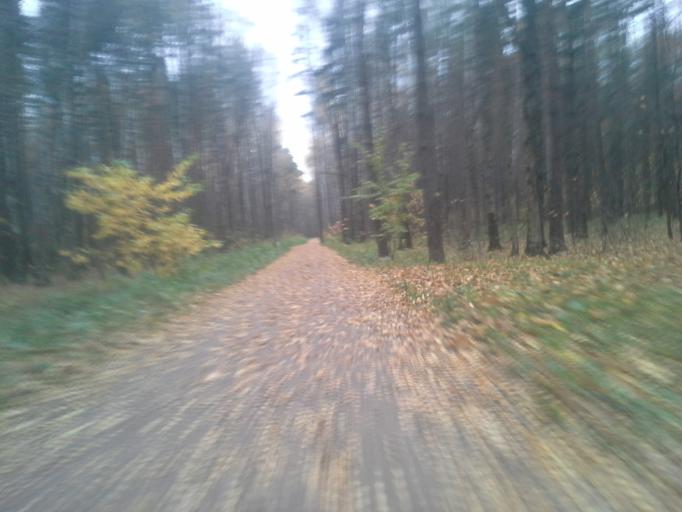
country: RU
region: Moskovskaya
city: Zarech'ye
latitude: 55.6663
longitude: 37.3946
